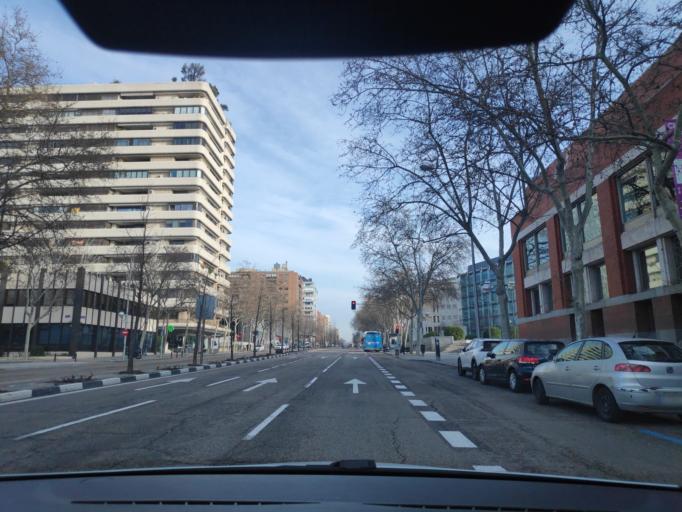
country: ES
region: Madrid
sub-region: Provincia de Madrid
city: Chamartin
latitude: 40.4463
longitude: -3.6756
